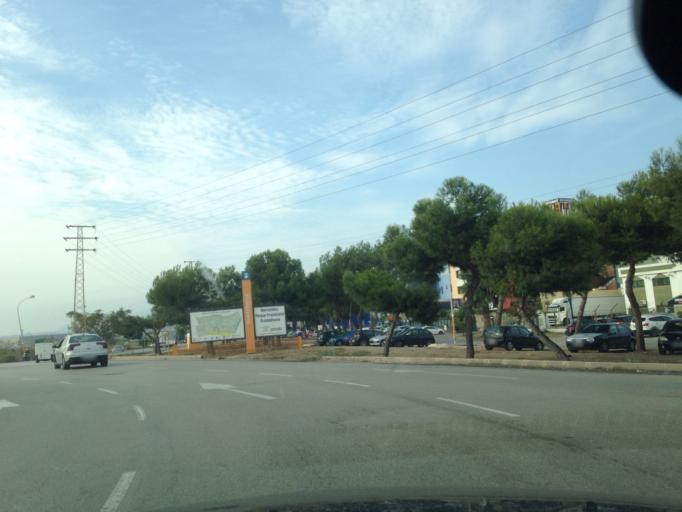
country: ES
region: Andalusia
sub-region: Provincia de Malaga
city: Malaga
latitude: 36.6919
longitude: -4.4656
